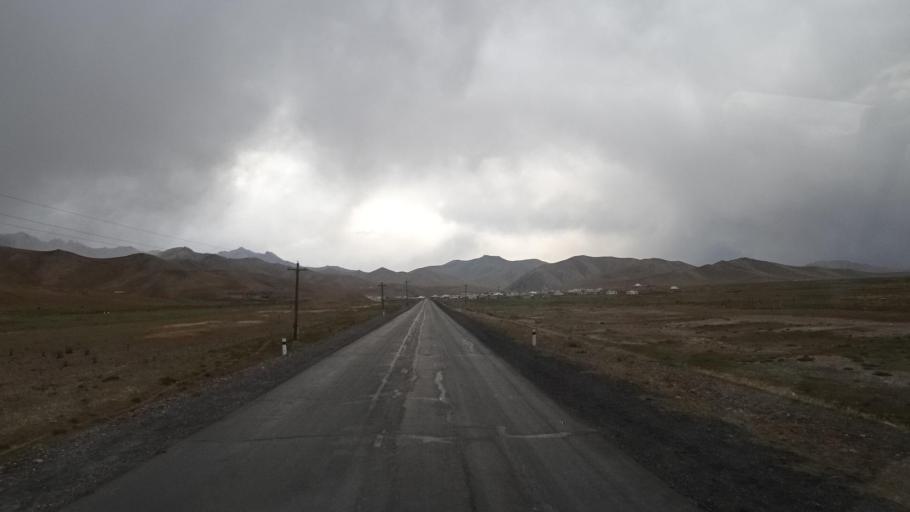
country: KG
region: Osh
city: Gul'cha
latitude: 39.7168
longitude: 73.2414
